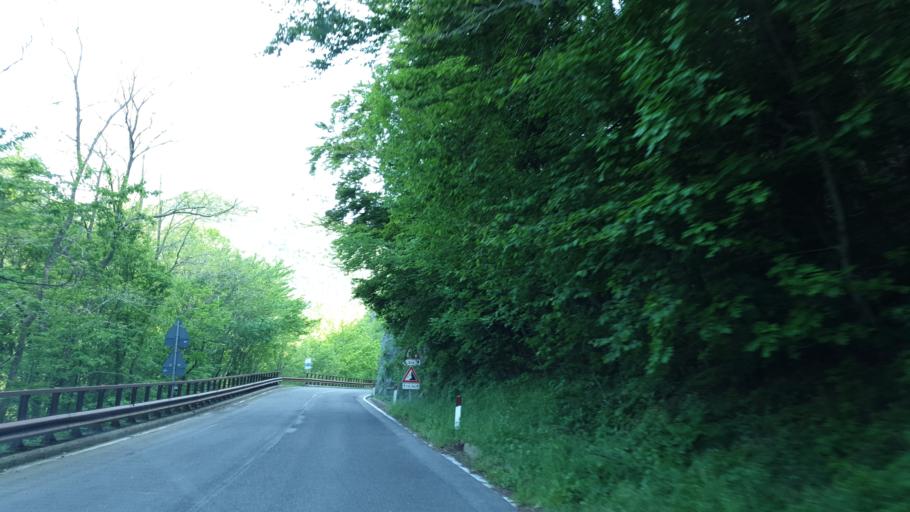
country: IT
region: Tuscany
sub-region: Province of Arezzo
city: Soci
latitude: 43.7786
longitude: 11.8691
